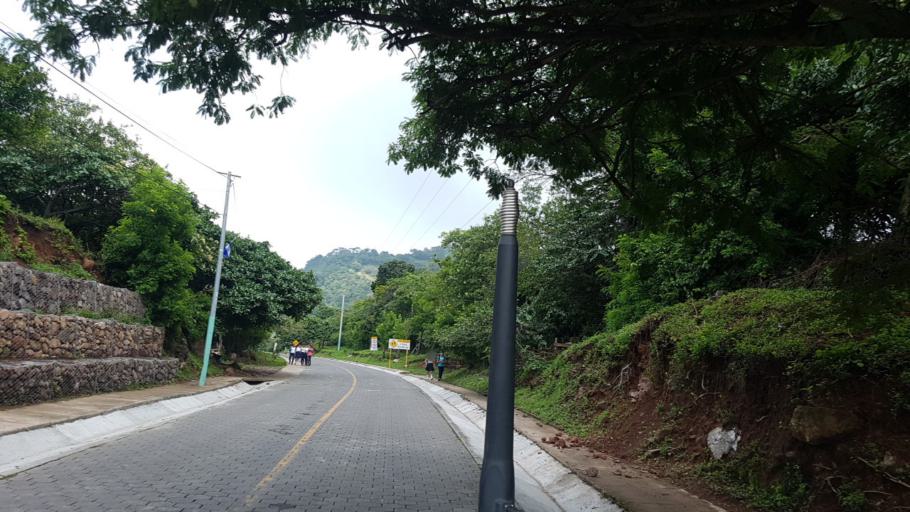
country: NI
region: Leon
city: Santa Rosa del Penon
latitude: 12.9319
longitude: -86.3441
